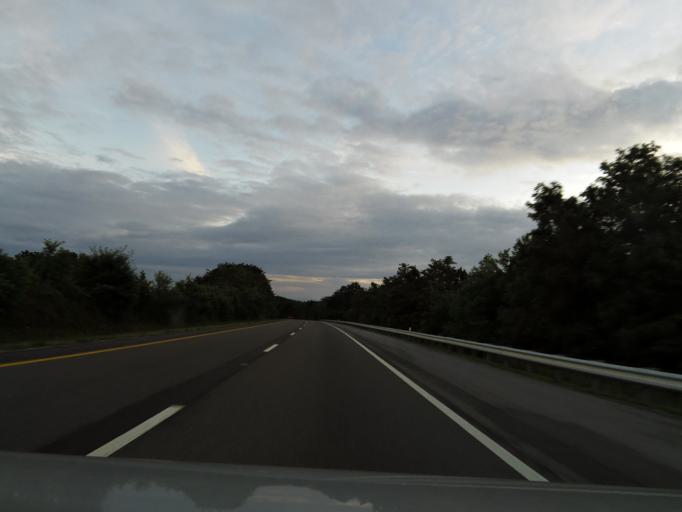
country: US
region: Tennessee
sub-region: Campbell County
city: Jellico
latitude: 36.5122
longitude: -84.1985
